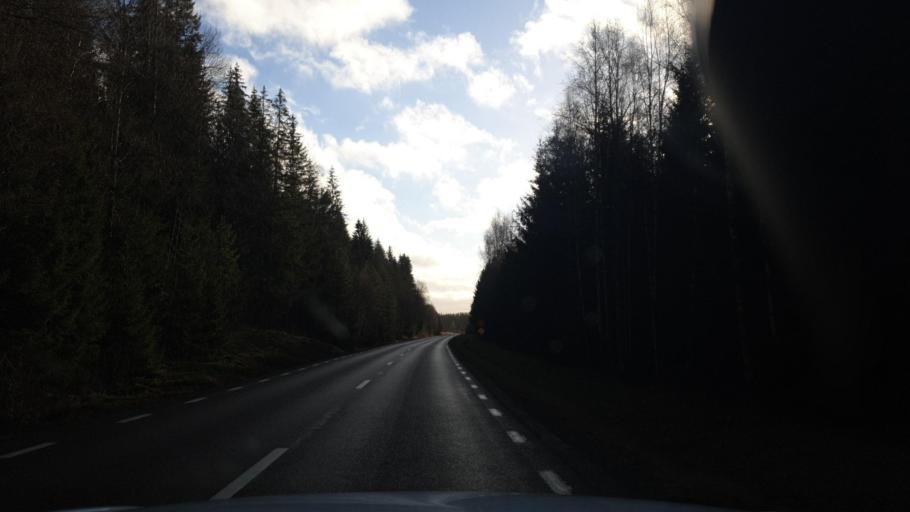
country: SE
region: Vaermland
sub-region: Arjangs Kommun
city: Arjaeng
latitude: 59.6223
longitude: 12.1432
